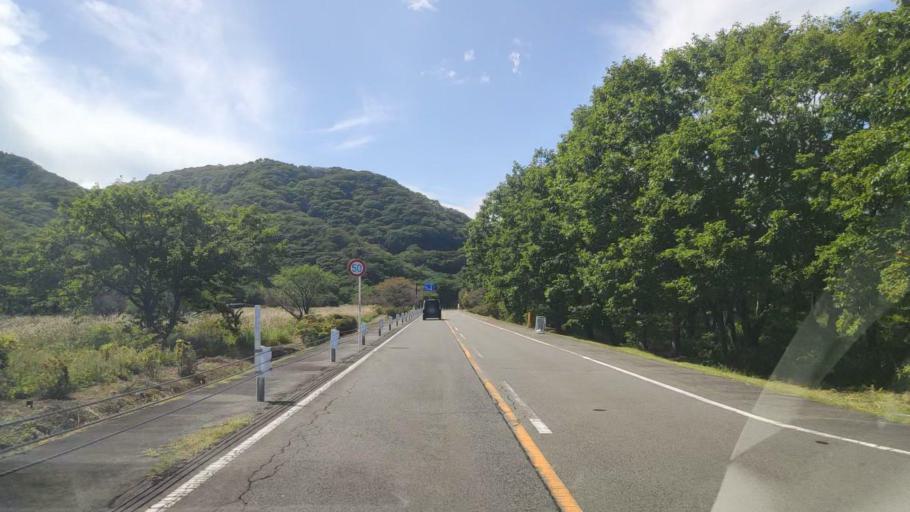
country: JP
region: Gunma
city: Shibukawa
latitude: 36.4714
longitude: 138.8836
